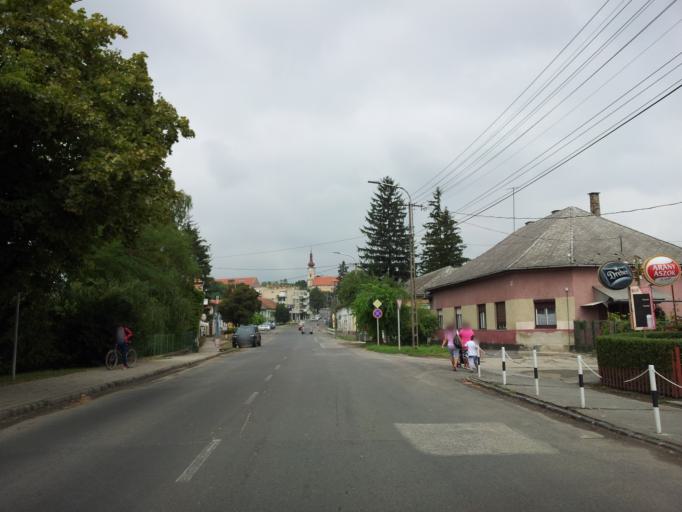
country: HU
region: Tolna
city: Tamasi
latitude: 46.6278
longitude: 18.2866
